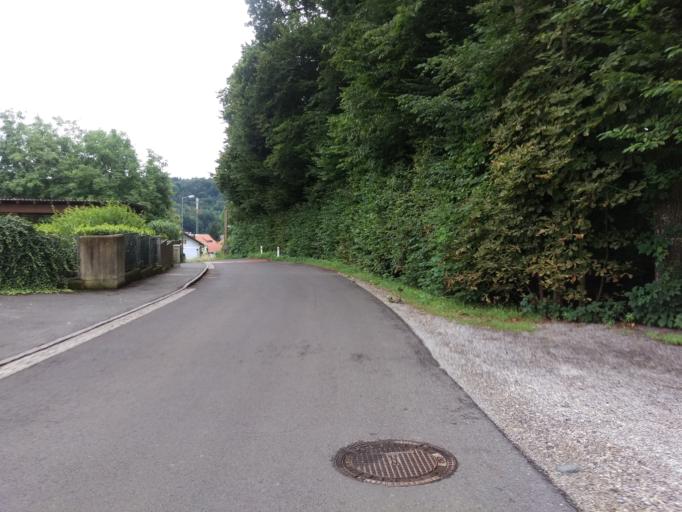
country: AT
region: Styria
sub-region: Politischer Bezirk Graz-Umgebung
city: Hart bei Graz
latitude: 47.0467
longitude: 15.5085
